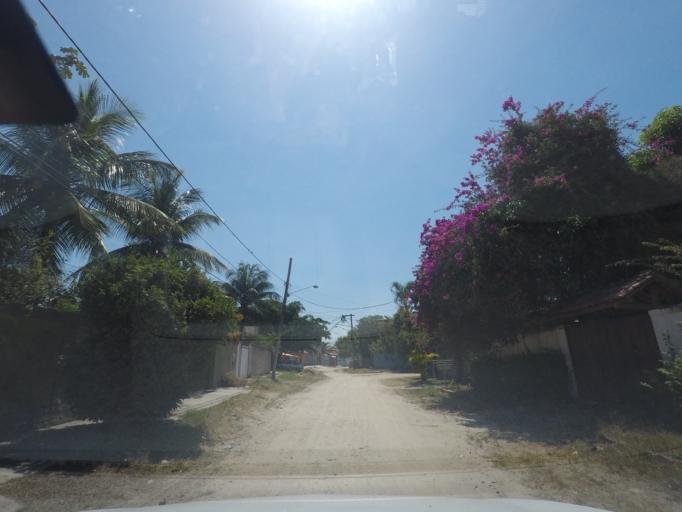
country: BR
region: Rio de Janeiro
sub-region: Niteroi
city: Niteroi
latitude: -22.9380
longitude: -43.0213
